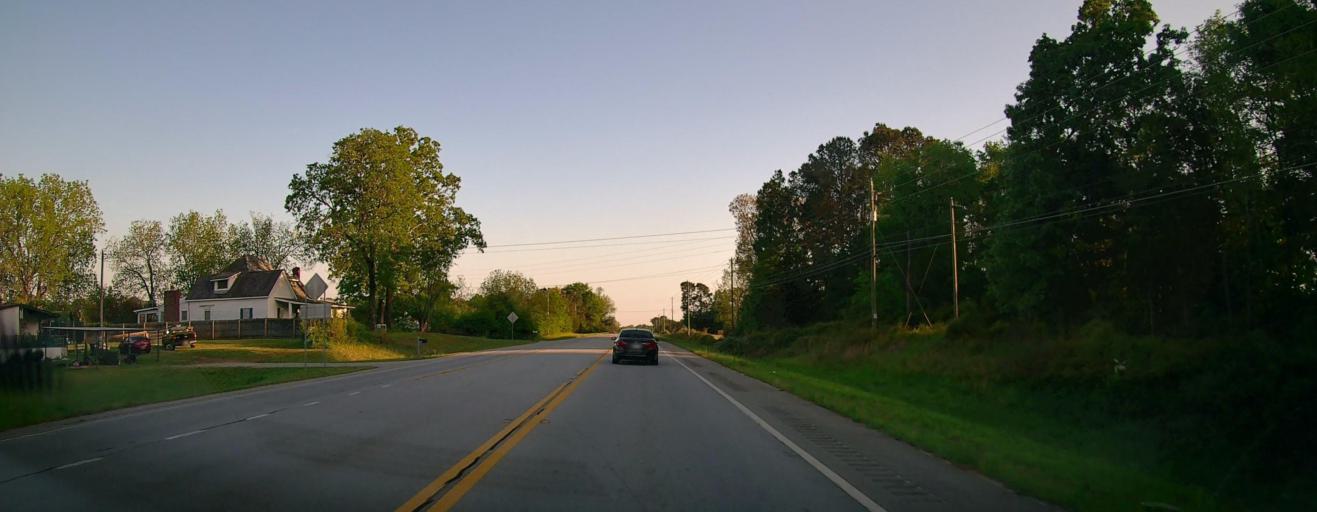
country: US
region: Georgia
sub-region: Newton County
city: Oakwood
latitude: 33.5353
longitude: -83.9523
